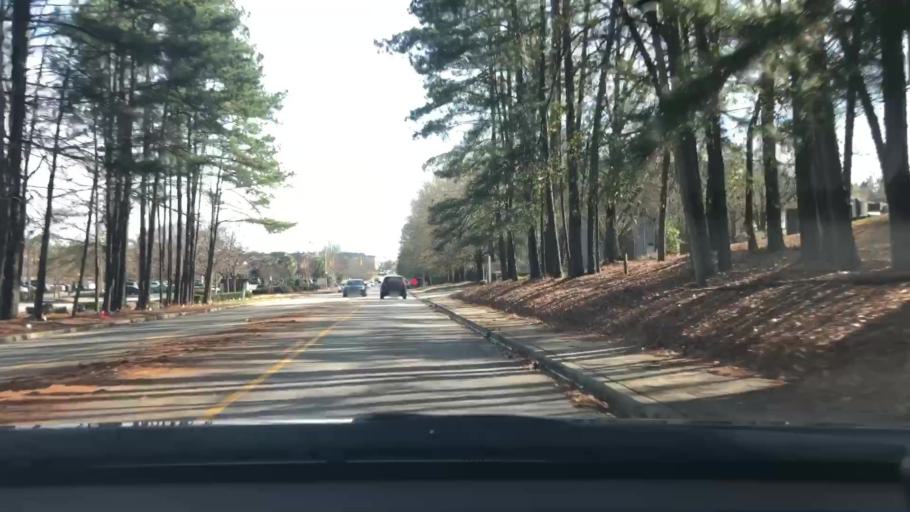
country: US
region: South Carolina
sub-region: Lexington County
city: Irmo
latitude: 34.0865
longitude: -81.1637
